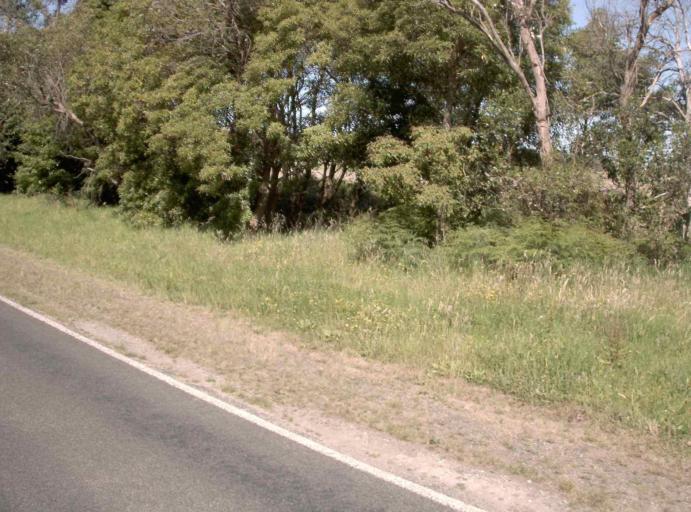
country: AU
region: Victoria
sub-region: Latrobe
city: Morwell
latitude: -38.6529
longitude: 146.4638
